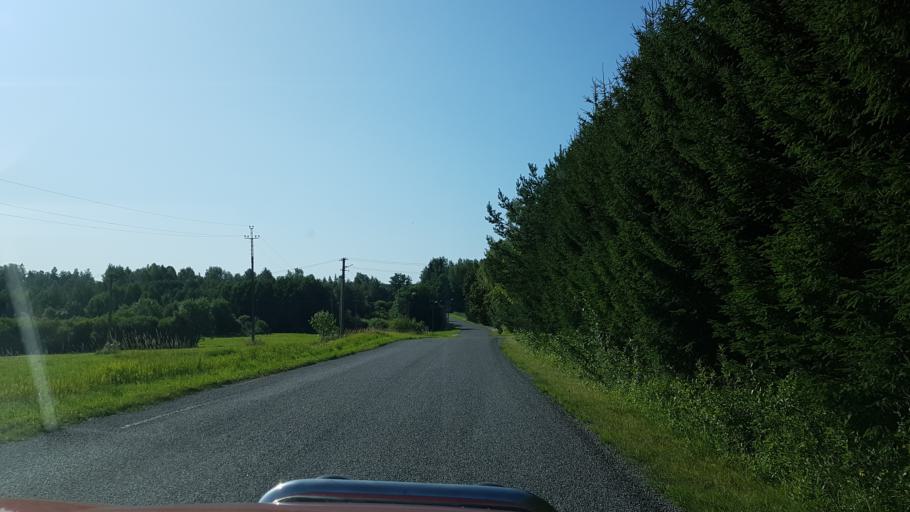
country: EE
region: Vorumaa
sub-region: Voru linn
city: Voru
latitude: 57.7357
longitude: 26.9272
